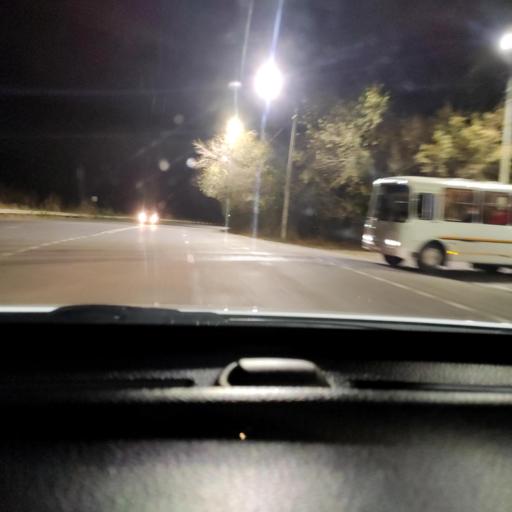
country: RU
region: Voronezj
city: Maslovka
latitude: 51.6298
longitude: 39.2866
